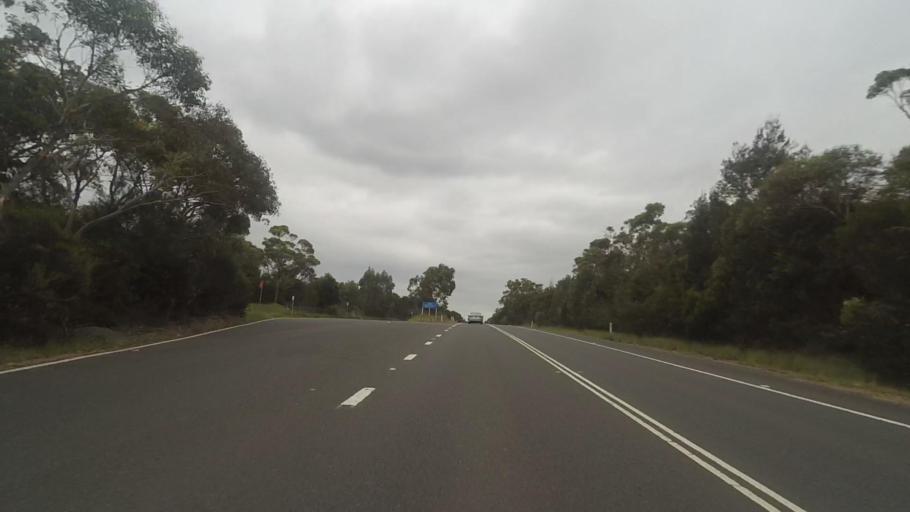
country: AU
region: New South Wales
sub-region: Sutherland Shire
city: Engadine
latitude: -34.0514
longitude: 150.9739
